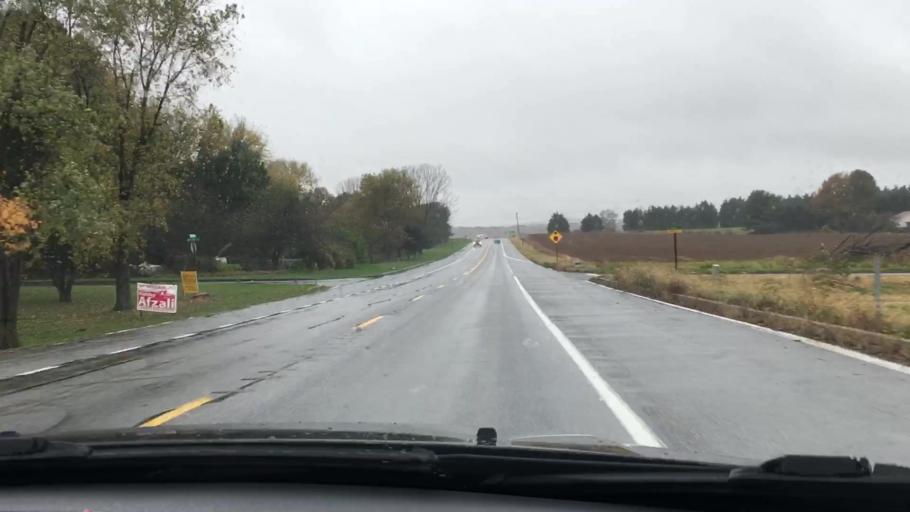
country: US
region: Maryland
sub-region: Frederick County
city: Buckeystown
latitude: 39.3219
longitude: -77.4333
